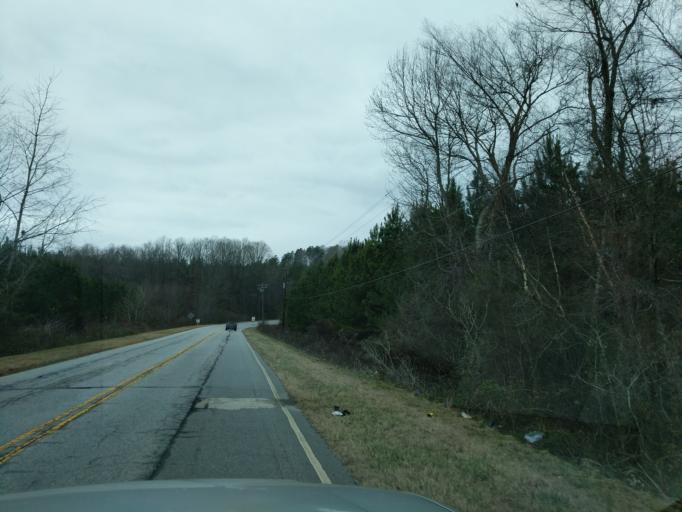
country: US
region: South Carolina
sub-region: Greenville County
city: Slater-Marietta
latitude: 35.0725
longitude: -82.5272
